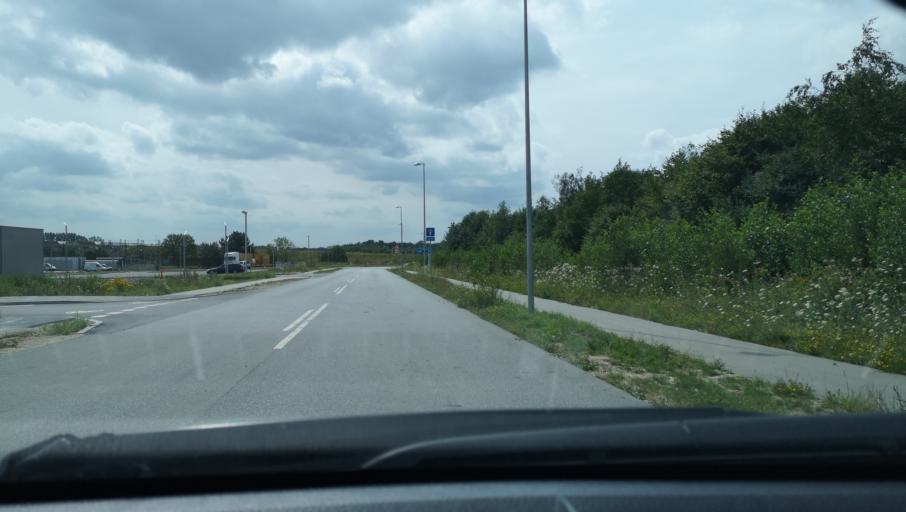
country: DK
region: Zealand
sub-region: Solrod Kommune
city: Solrod
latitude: 55.5001
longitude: 12.1706
